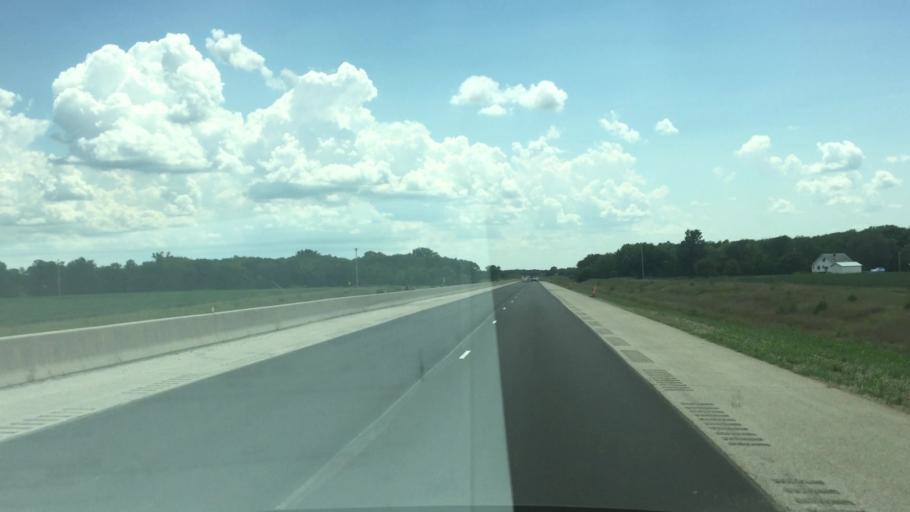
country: US
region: Kansas
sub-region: Lyon County
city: Emporia
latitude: 38.5234
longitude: -96.1410
